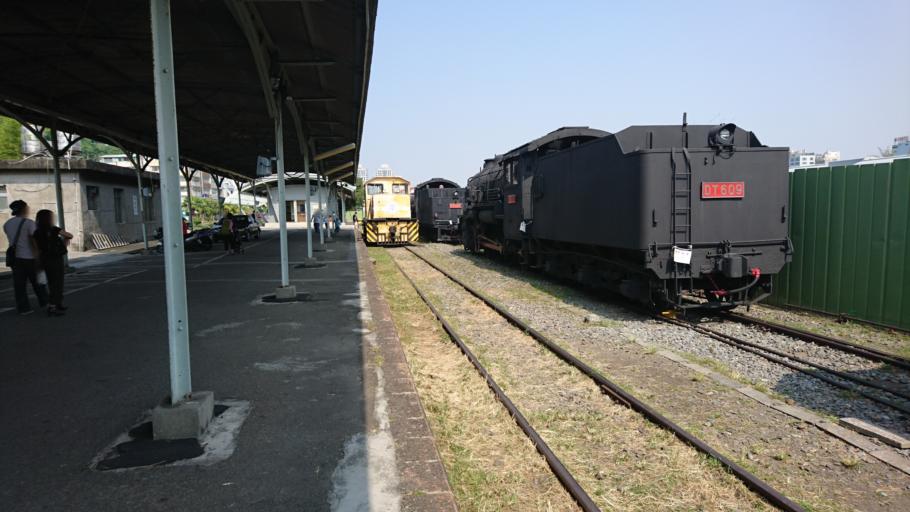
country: TW
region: Kaohsiung
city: Kaohsiung
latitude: 22.6216
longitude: 120.2757
